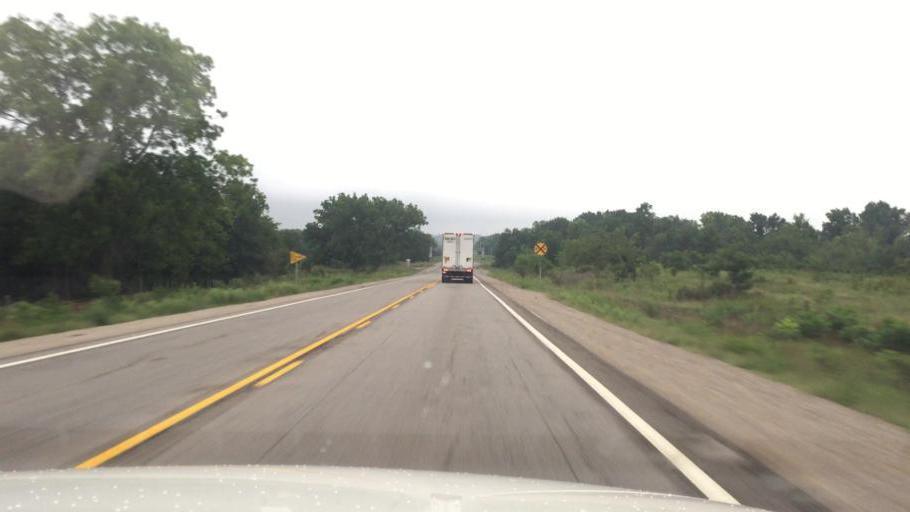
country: US
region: Kansas
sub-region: Montgomery County
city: Cherryvale
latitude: 37.1870
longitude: -95.5794
